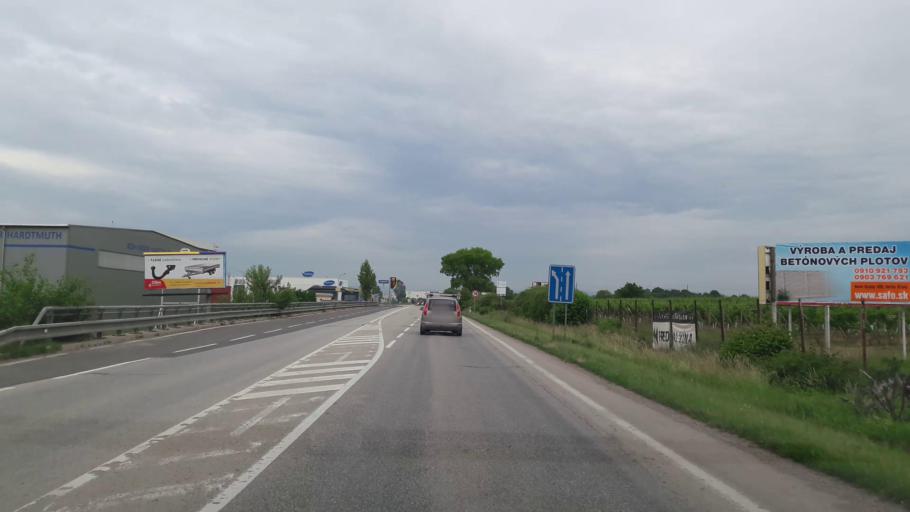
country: SK
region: Bratislavsky
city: Senec
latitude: 48.2298
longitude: 17.3762
